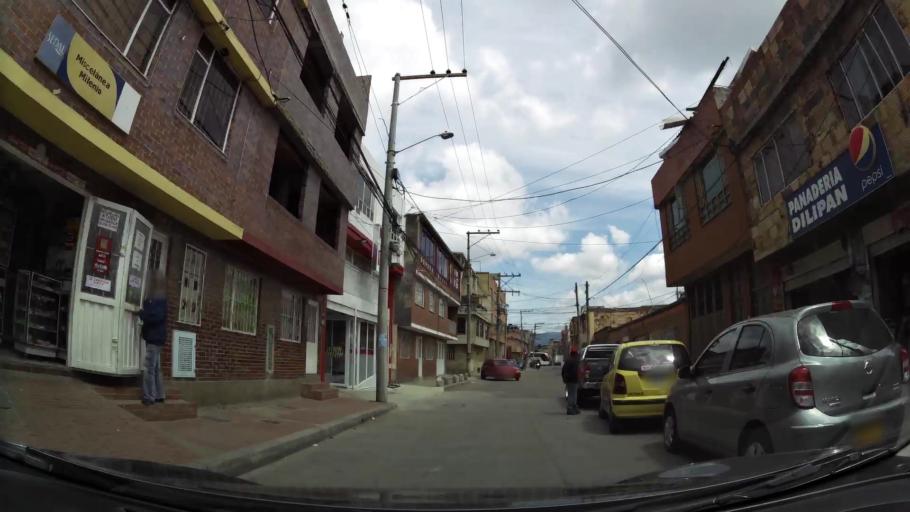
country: CO
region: Cundinamarca
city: Cota
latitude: 4.7262
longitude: -74.0987
